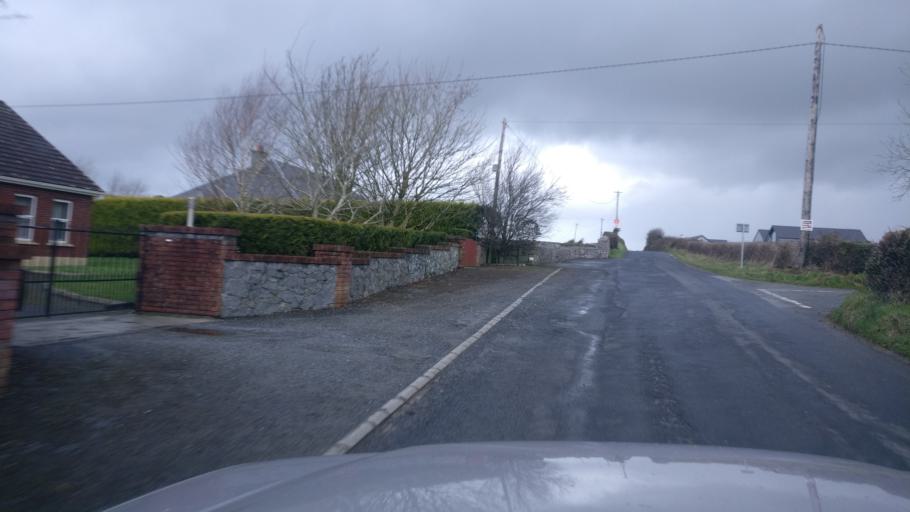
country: IE
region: Connaught
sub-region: County Galway
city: Loughrea
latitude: 53.1754
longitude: -8.6934
